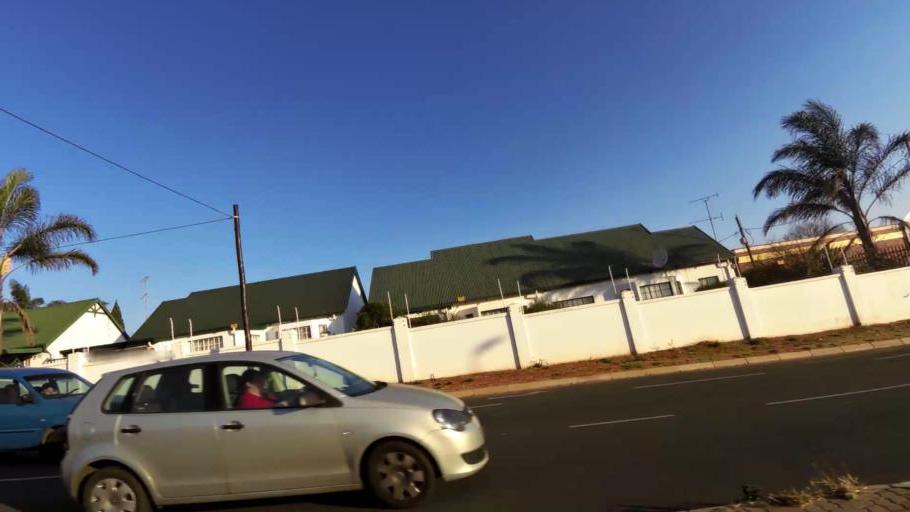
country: ZA
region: Gauteng
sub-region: City of Johannesburg Metropolitan Municipality
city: Roodepoort
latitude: -26.1643
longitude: 27.9456
